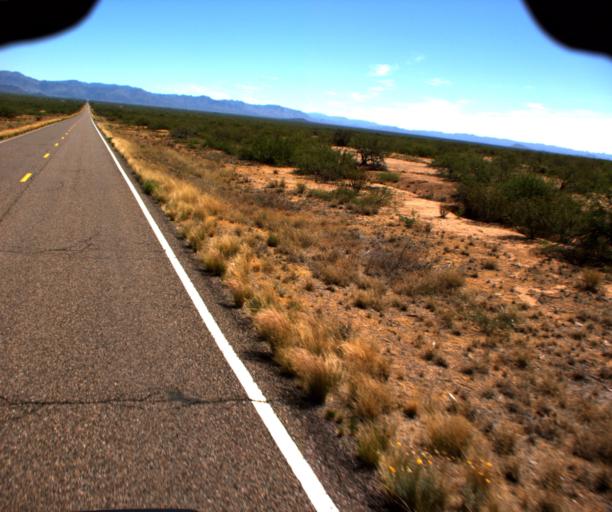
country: US
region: Arizona
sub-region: Yavapai County
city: Congress
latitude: 34.1099
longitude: -112.9846
